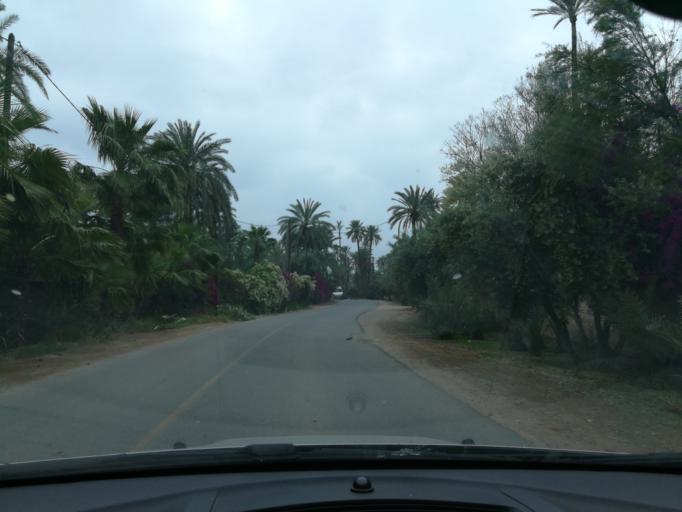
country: MA
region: Marrakech-Tensift-Al Haouz
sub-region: Marrakech
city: Marrakesh
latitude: 31.6722
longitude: -7.9841
